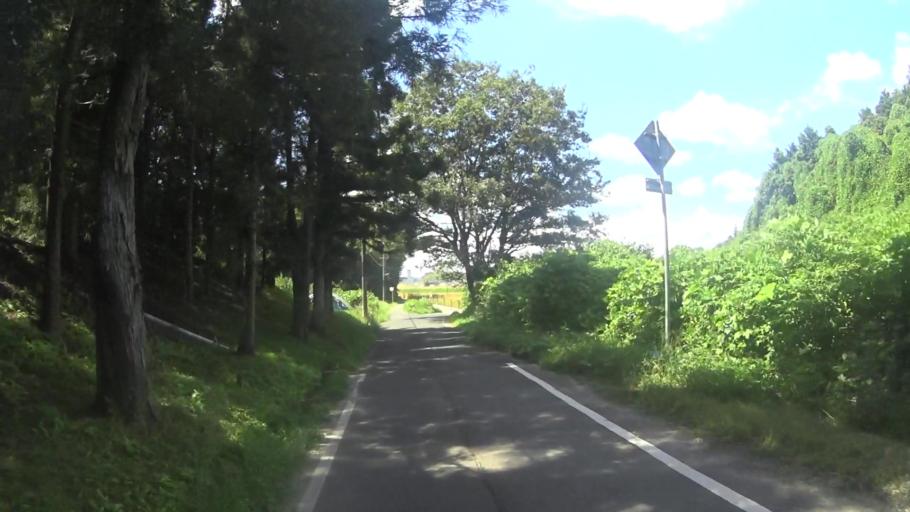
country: JP
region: Nara
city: Nara-shi
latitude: 34.7332
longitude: 135.8501
